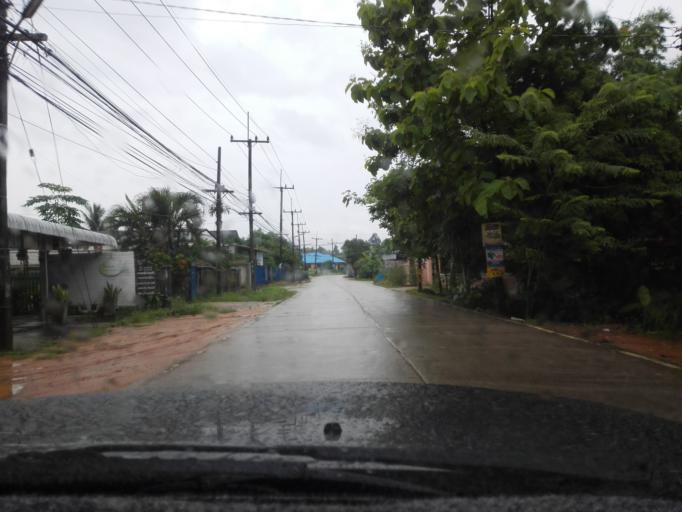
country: TH
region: Tak
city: Mae Sot
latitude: 16.6811
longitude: 98.5779
